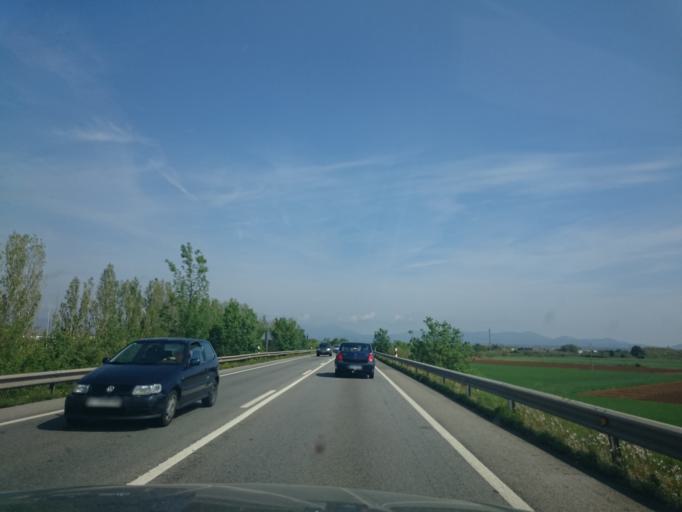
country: ES
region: Catalonia
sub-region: Provincia de Girona
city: Vilabertran
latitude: 42.2594
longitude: 2.9863
